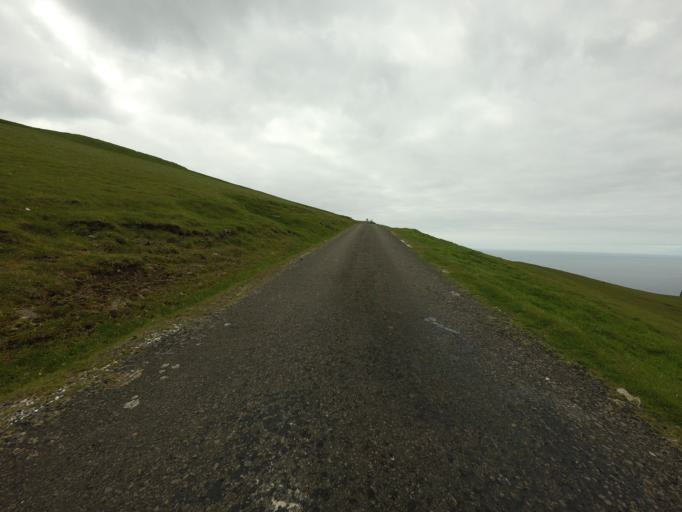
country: FO
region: Suduroy
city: Vagur
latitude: 61.4249
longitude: -6.7552
